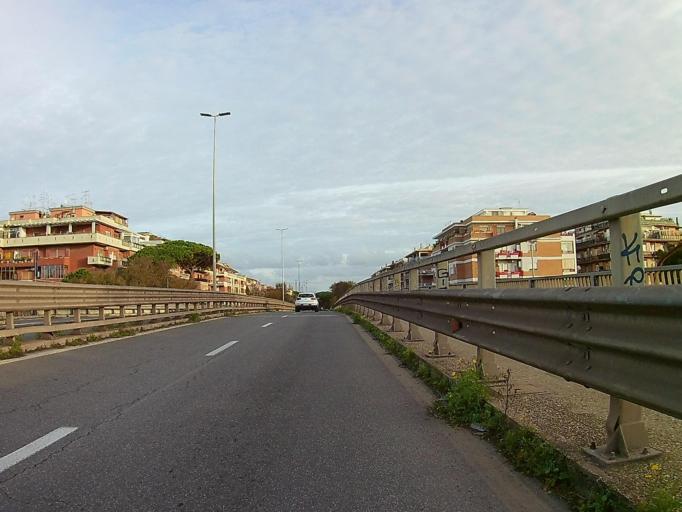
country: IT
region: Latium
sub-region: Citta metropolitana di Roma Capitale
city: Lido di Ostia
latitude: 41.7375
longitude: 12.2820
